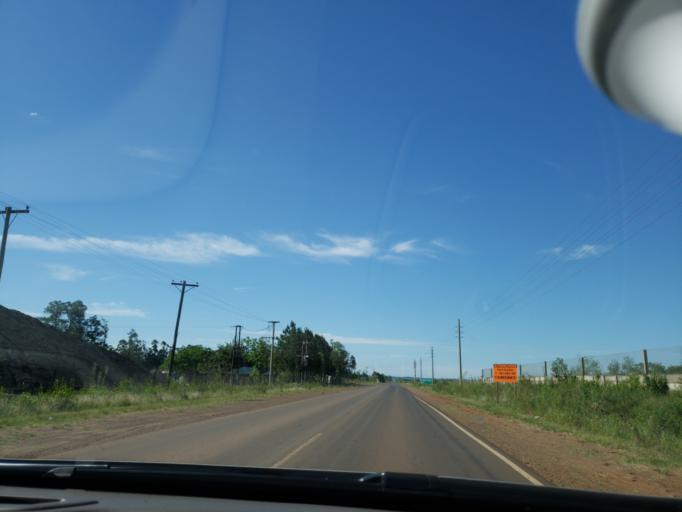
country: AR
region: Misiones
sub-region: Departamento de Capital
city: Posadas
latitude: -27.3898
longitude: -55.9752
